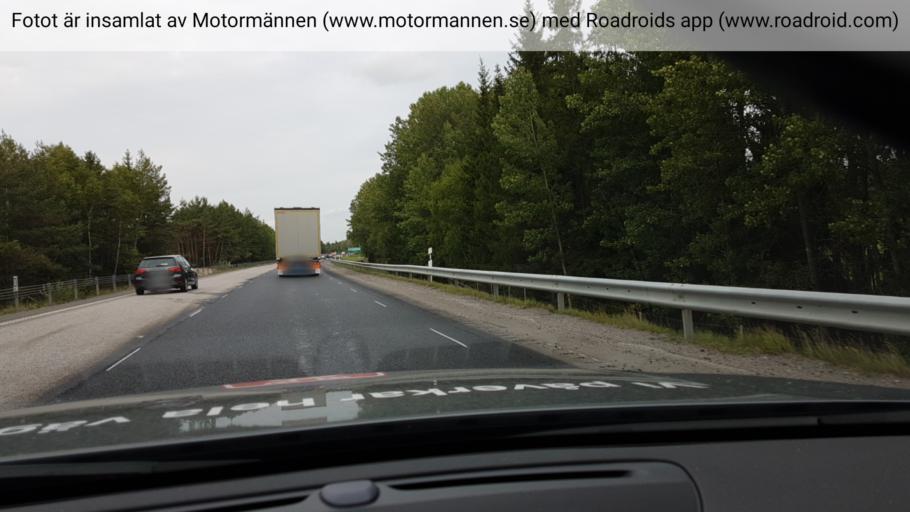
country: SE
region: Uppsala
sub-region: Knivsta Kommun
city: Knivsta
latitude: 59.7663
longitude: 17.7911
